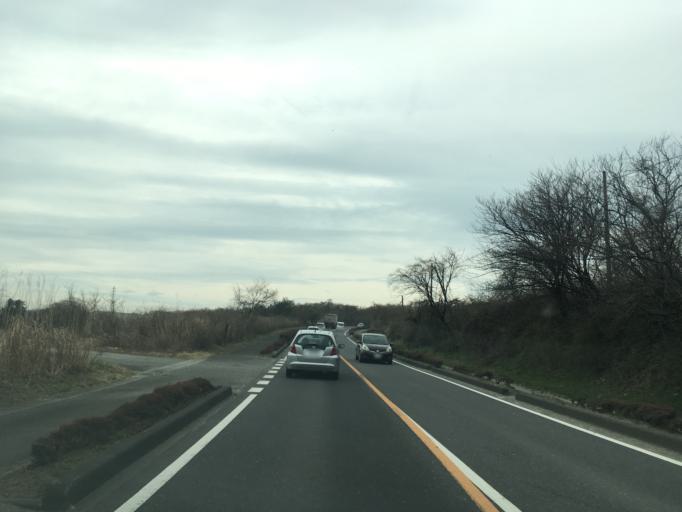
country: JP
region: Tochigi
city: Kuroiso
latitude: 37.0370
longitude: 139.9914
